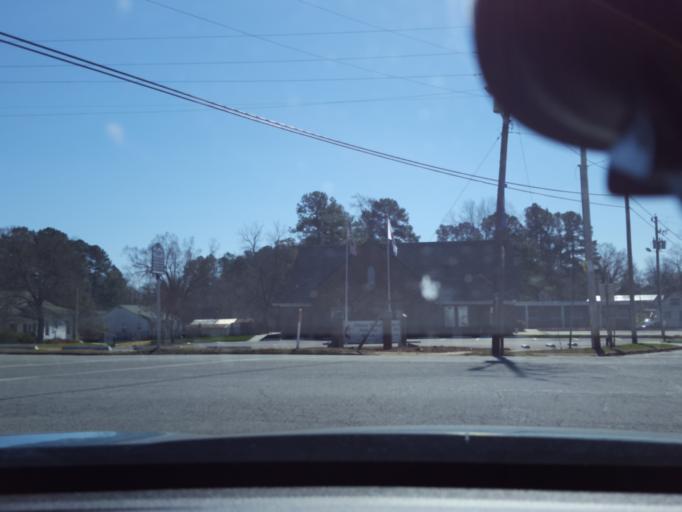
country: US
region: North Carolina
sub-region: Halifax County
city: South Rosemary
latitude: 36.4347
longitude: -77.9120
